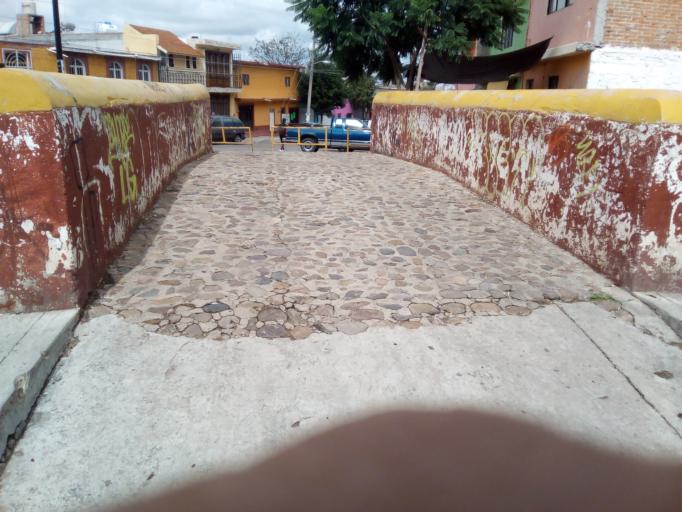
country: MX
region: Guerrero
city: San Luis de la Paz
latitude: 21.2944
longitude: -100.5104
